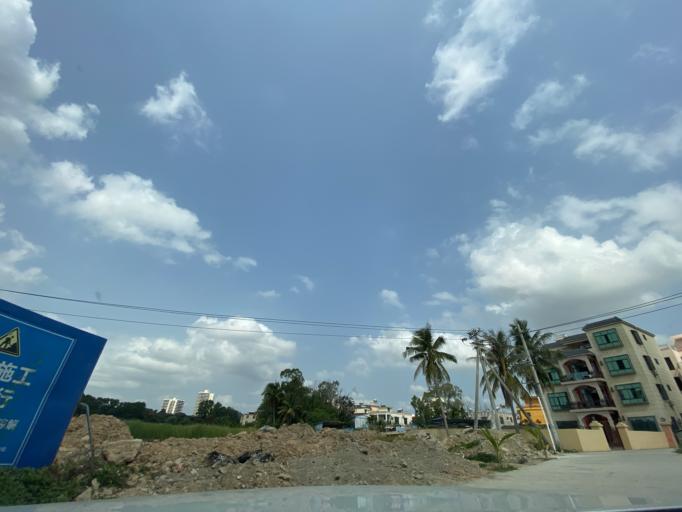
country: CN
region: Hainan
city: Yingzhou
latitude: 18.4166
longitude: 109.8479
